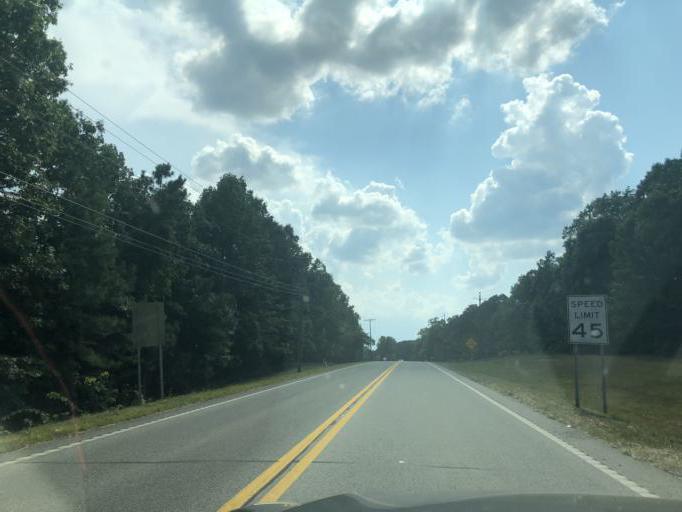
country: US
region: Tennessee
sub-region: Franklin County
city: Sewanee
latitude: 35.2105
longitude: -85.8972
